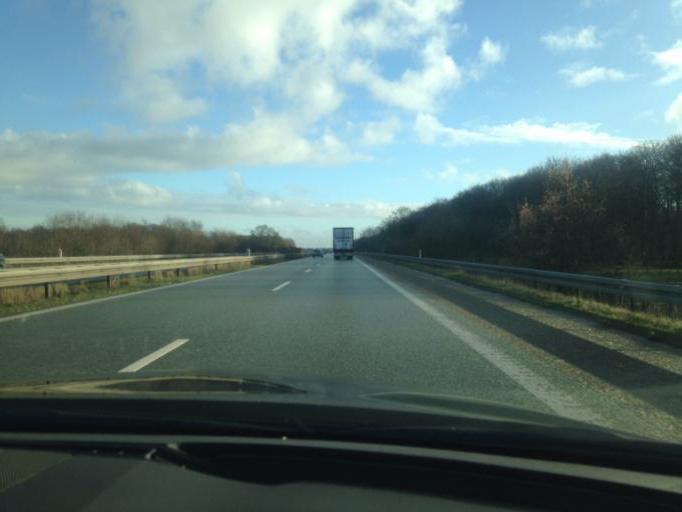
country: DK
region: South Denmark
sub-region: Vejen Kommune
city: Vejen
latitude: 55.4983
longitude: 9.0795
